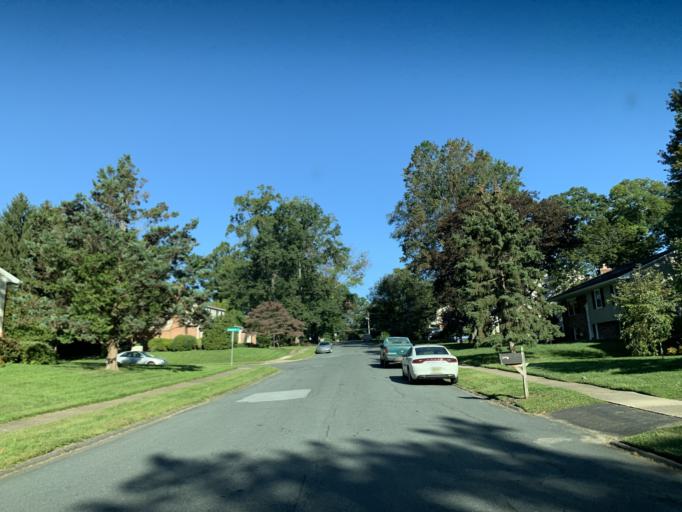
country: US
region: Maryland
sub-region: Harford County
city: Bel Air North
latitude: 39.5528
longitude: -76.3736
